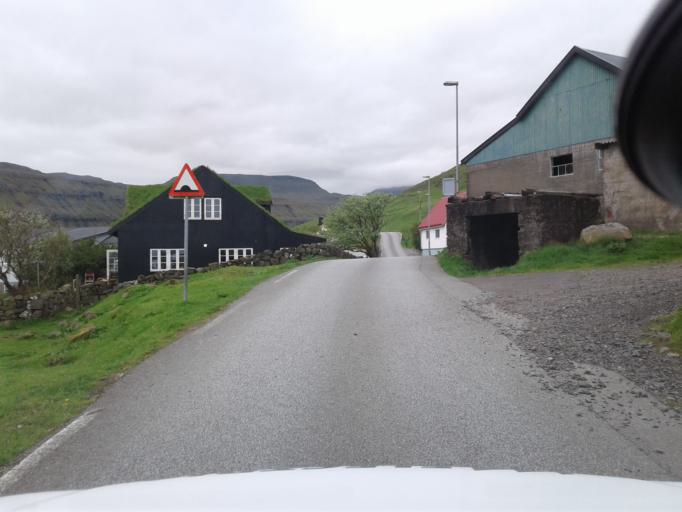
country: FO
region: Streymoy
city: Hoyvik
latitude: 62.0583
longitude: -6.8338
